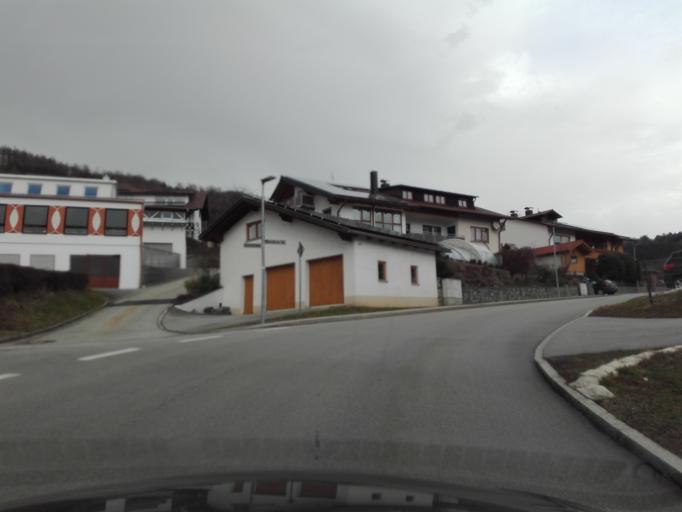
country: DE
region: Bavaria
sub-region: Lower Bavaria
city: Obernzell
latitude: 48.5577
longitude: 13.6338
